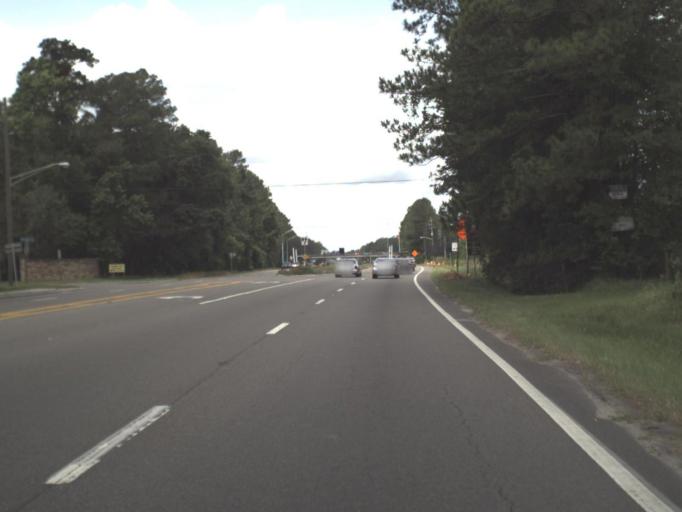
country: US
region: Florida
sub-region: Nassau County
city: Nassau Village-Ratliff
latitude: 30.4385
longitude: -81.7171
